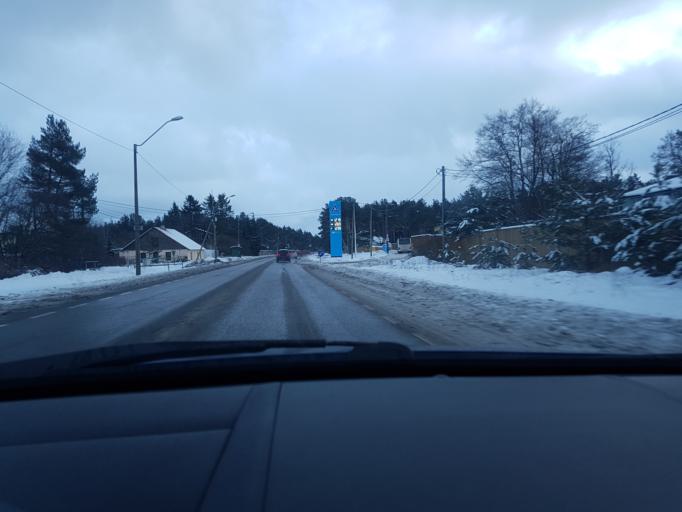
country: EE
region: Harju
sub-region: Tallinna linn
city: Tallinn
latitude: 59.3634
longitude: 24.7629
